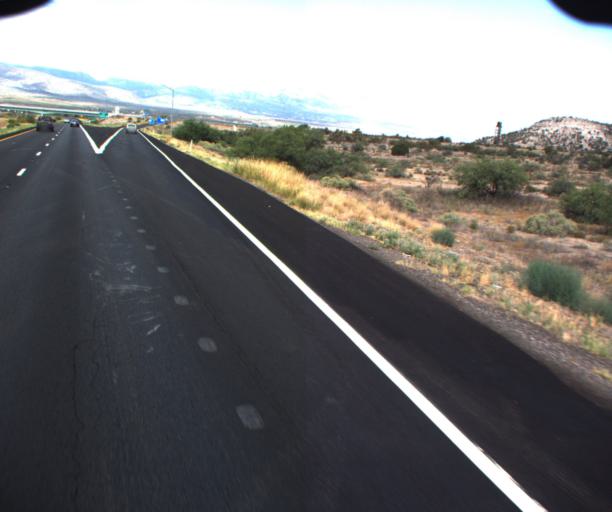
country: US
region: Arizona
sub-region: Yavapai County
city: Camp Verde
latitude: 34.6126
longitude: -111.8576
